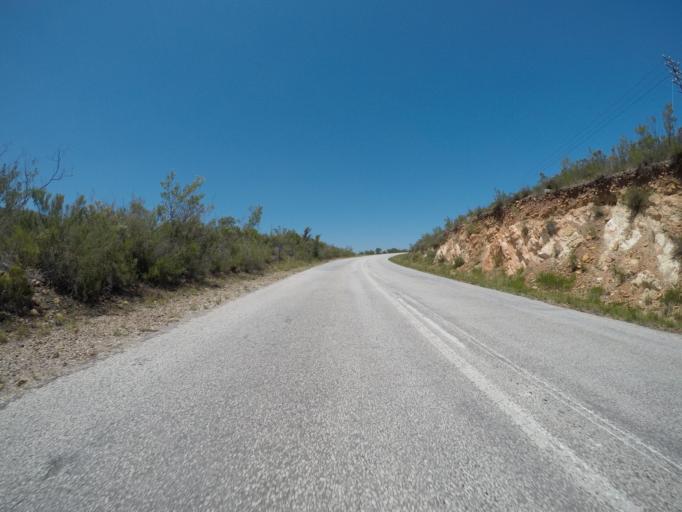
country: ZA
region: Eastern Cape
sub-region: Cacadu District Municipality
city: Kareedouw
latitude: -33.8857
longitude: 24.0807
